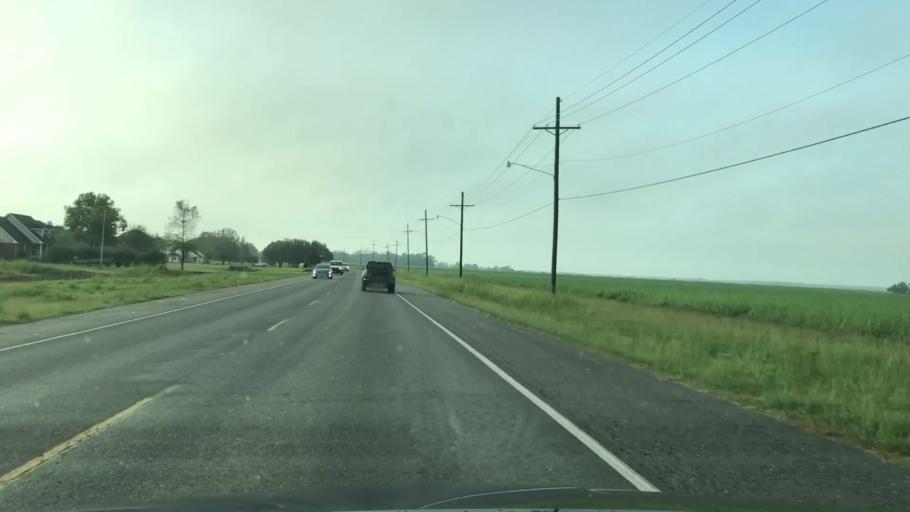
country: US
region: Louisiana
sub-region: Terrebonne Parish
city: Gray
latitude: 29.6619
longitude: -90.8204
